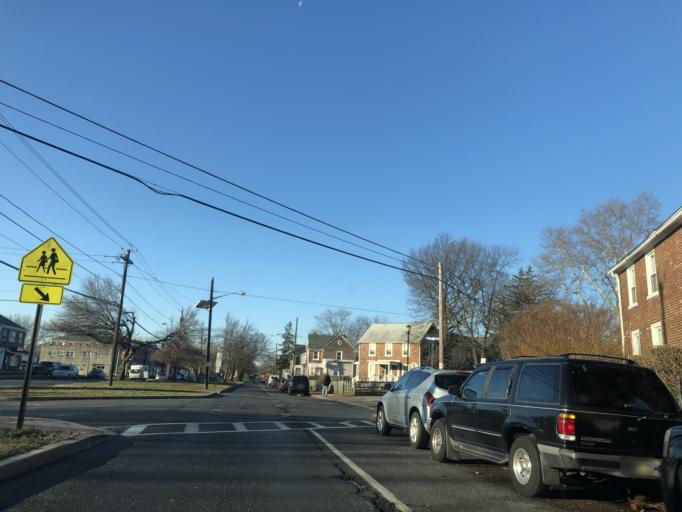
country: US
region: New Jersey
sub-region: Camden County
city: Wood-Lynne
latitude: 39.9052
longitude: -75.1019
